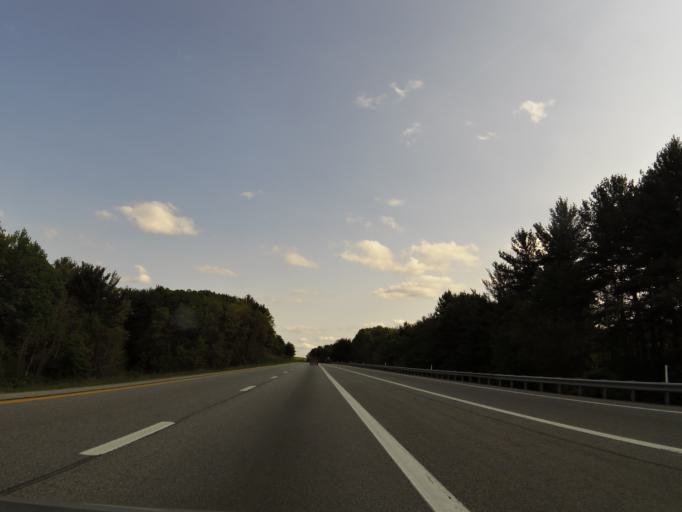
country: US
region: West Virginia
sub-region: Mercer County
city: Athens
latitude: 37.4213
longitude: -81.0663
